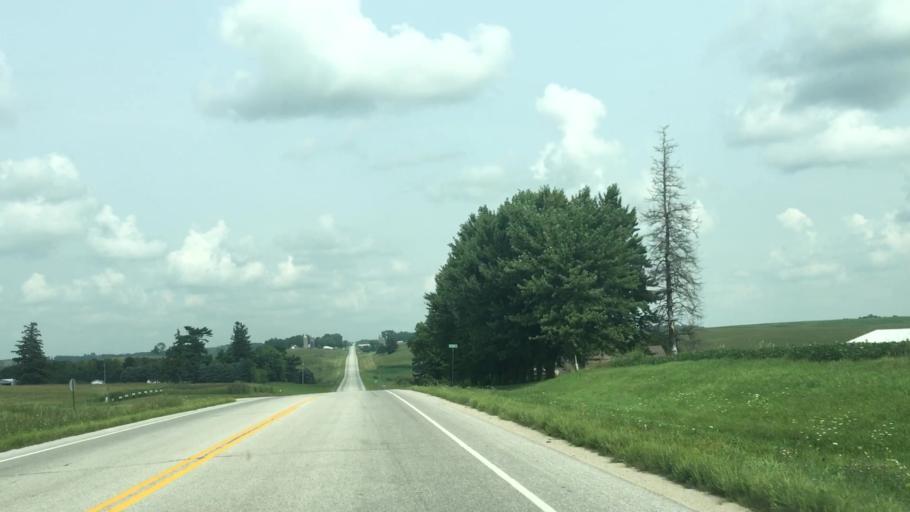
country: US
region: Minnesota
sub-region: Fillmore County
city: Harmony
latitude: 43.6014
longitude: -91.9296
